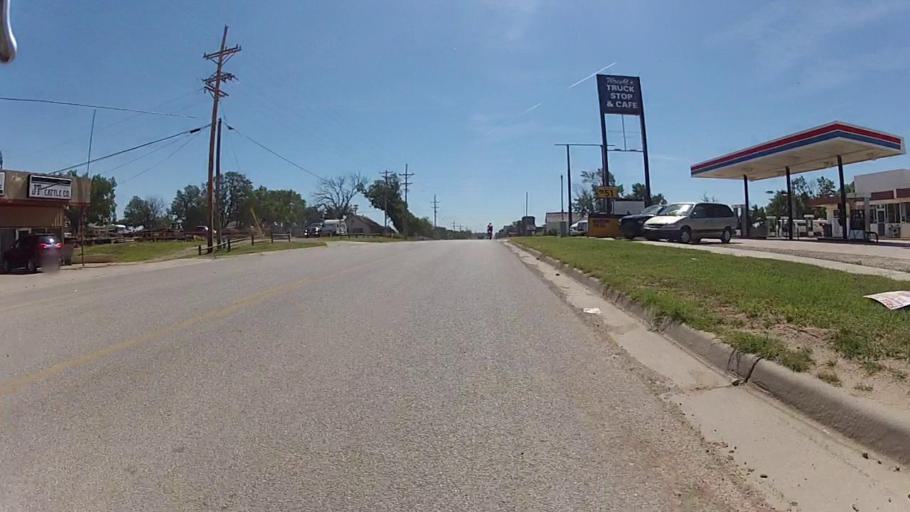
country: US
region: Kansas
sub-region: Barber County
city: Medicine Lodge
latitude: 37.2757
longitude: -98.5824
